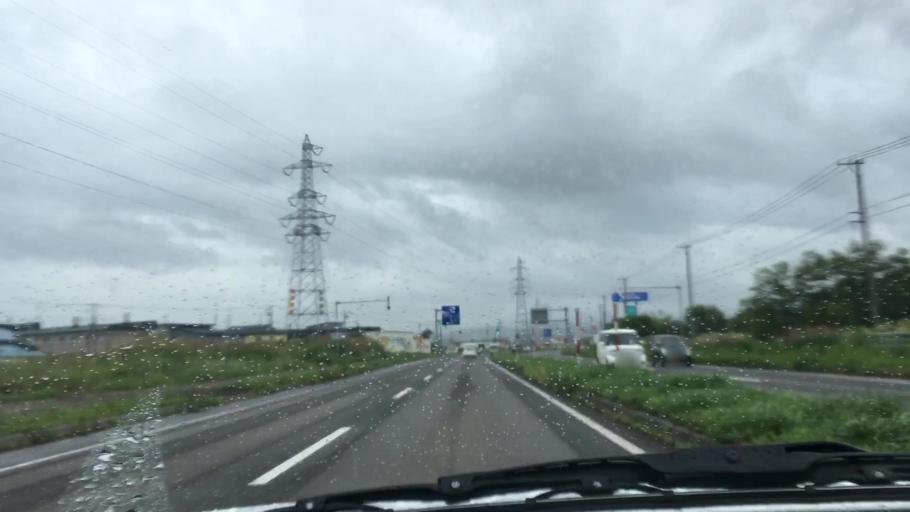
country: JP
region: Hokkaido
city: Nanae
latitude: 42.2555
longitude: 140.2815
